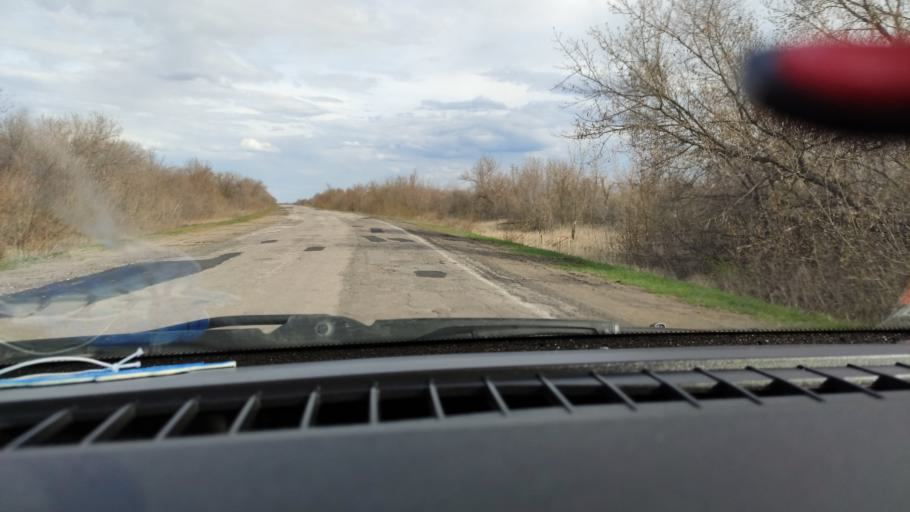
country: RU
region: Saratov
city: Rovnoye
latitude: 51.0694
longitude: 45.9938
